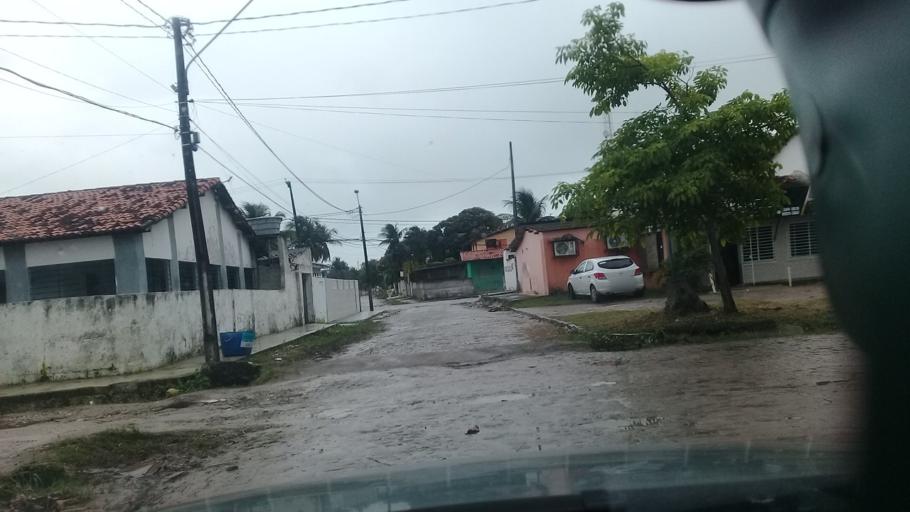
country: BR
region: Pernambuco
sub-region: Itamaraca
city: Itamaraca
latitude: -7.7551
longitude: -34.8265
